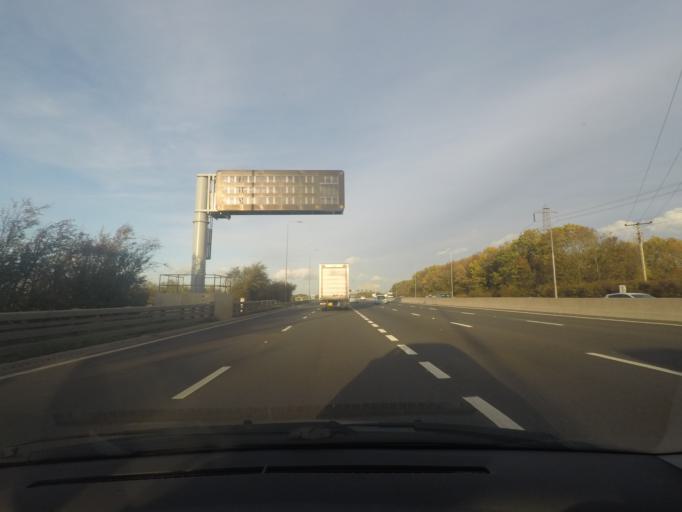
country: GB
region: England
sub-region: City and Borough of Leeds
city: Lofthouse
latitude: 53.7207
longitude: -1.5256
